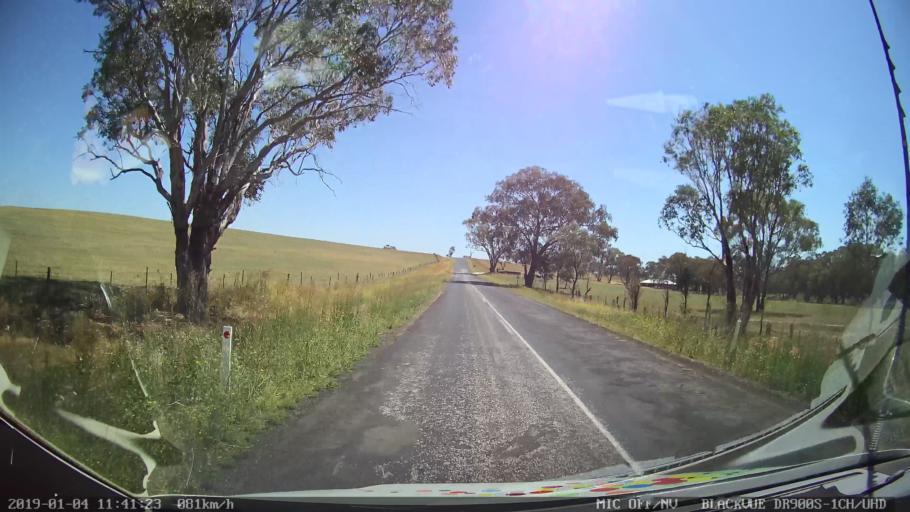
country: AU
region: New South Wales
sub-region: Cabonne
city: Molong
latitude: -32.9943
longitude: 148.7875
